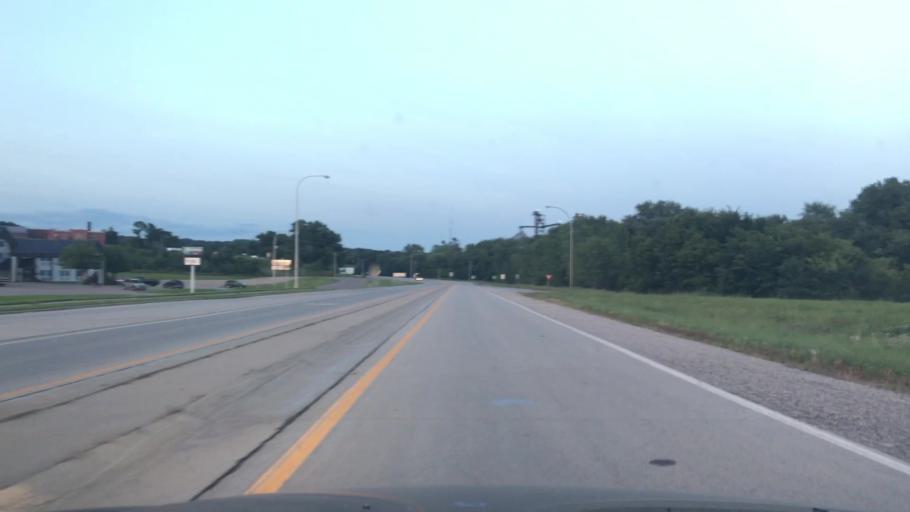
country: US
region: Minnesota
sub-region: Redwood County
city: Redwood Falls
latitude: 44.5491
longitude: -94.9947
